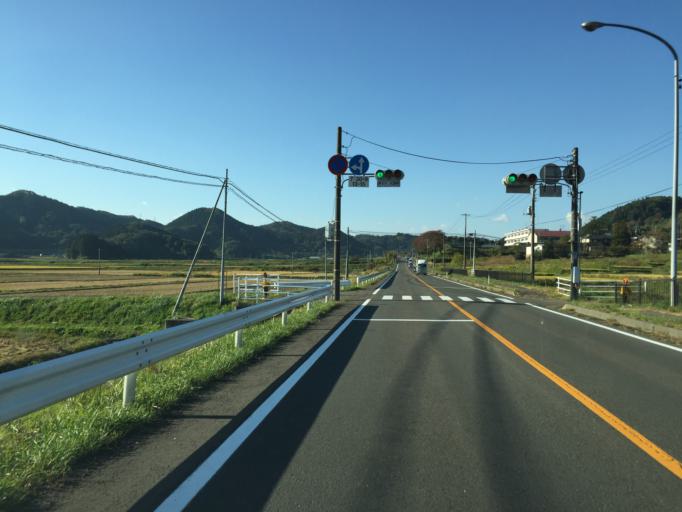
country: JP
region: Fukushima
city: Yanagawamachi-saiwaicho
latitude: 37.9241
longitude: 140.6008
